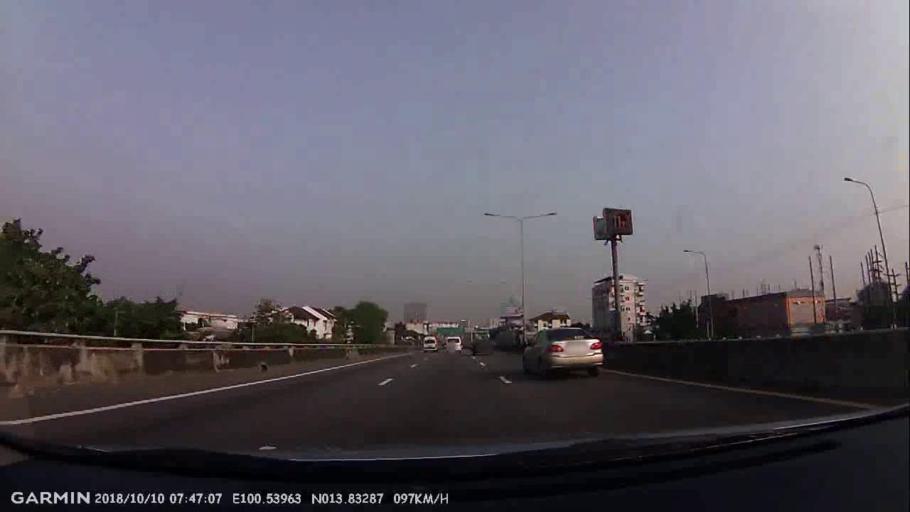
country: TH
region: Bangkok
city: Chatuchak
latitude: 13.8328
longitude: 100.5392
